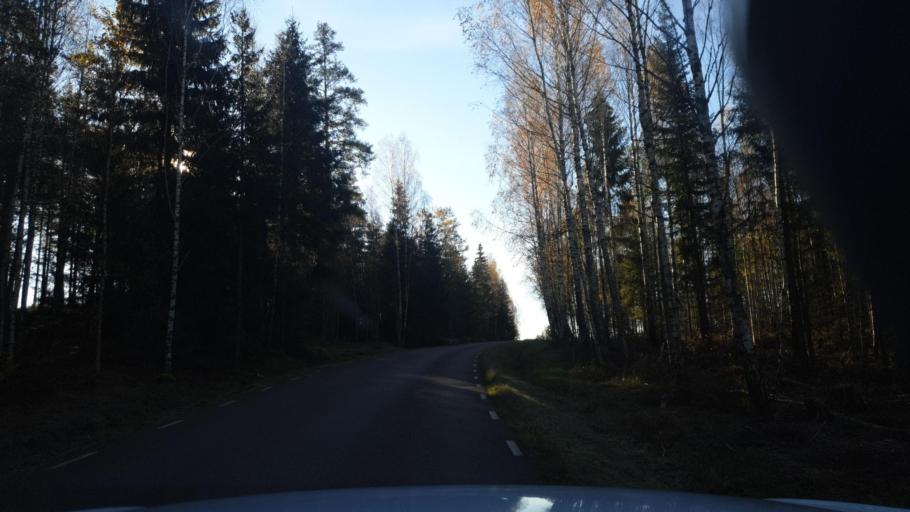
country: SE
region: Vaermland
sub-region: Grums Kommun
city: Grums
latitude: 59.4261
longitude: 13.0867
